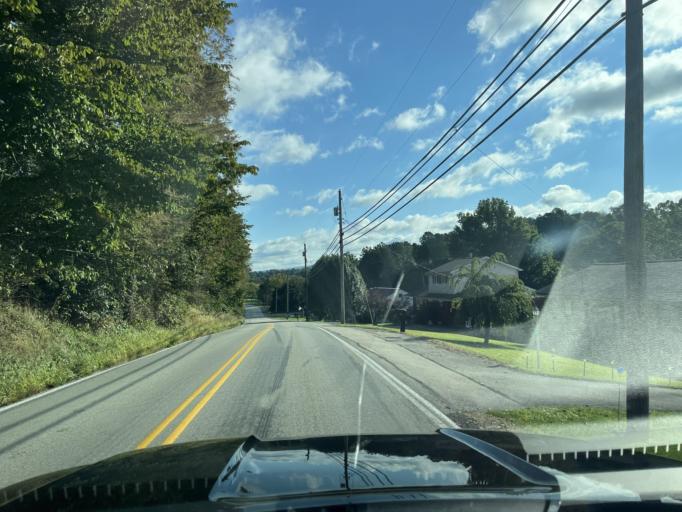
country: US
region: Pennsylvania
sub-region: Fayette County
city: South Uniontown
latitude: 39.8808
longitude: -79.7579
